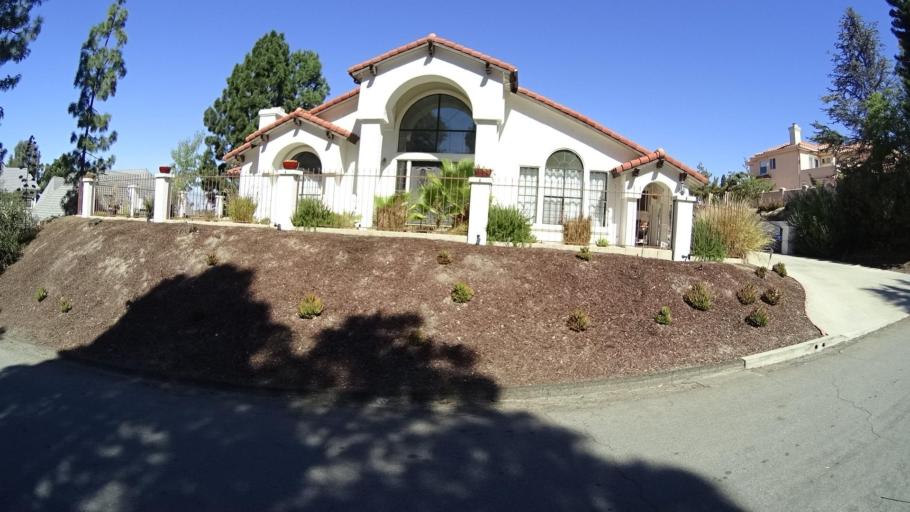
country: US
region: California
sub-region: San Diego County
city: Bonita
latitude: 32.6595
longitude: -117.0120
